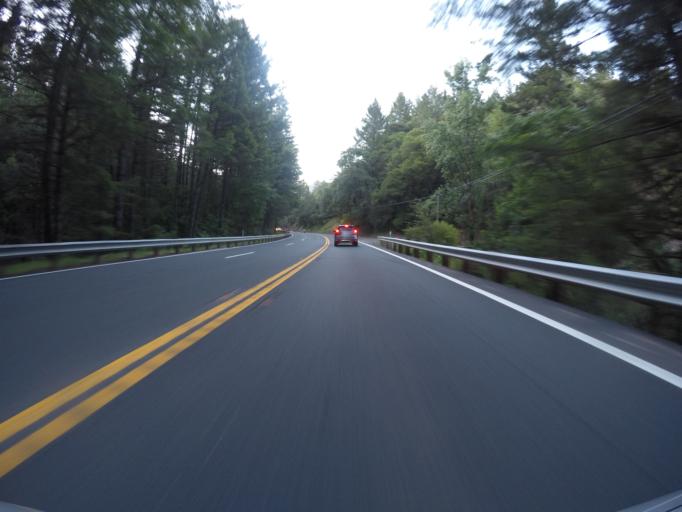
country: US
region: California
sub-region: Mendocino County
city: Laytonville
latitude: 39.7911
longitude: -123.5426
